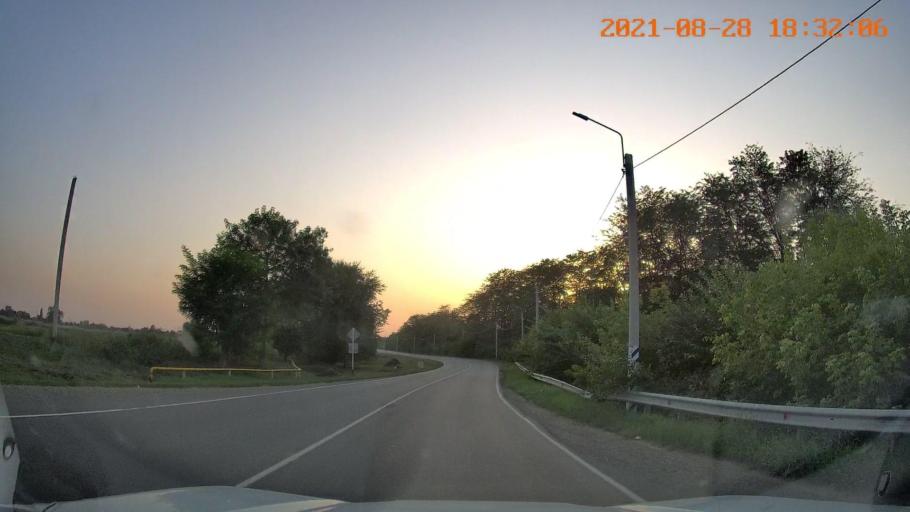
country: RU
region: Adygeya
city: Giaginskaya
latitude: 44.8775
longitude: 40.1945
